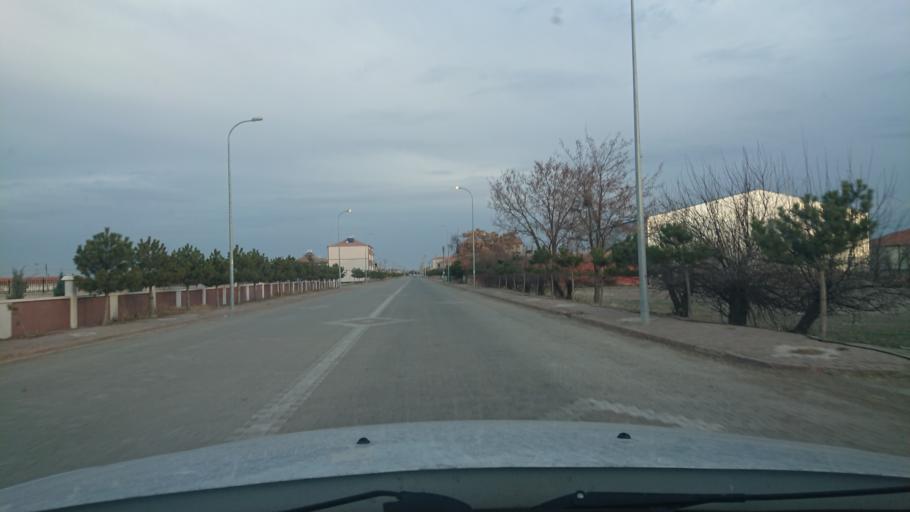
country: TR
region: Aksaray
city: Yesilova
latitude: 38.3335
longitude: 33.7517
